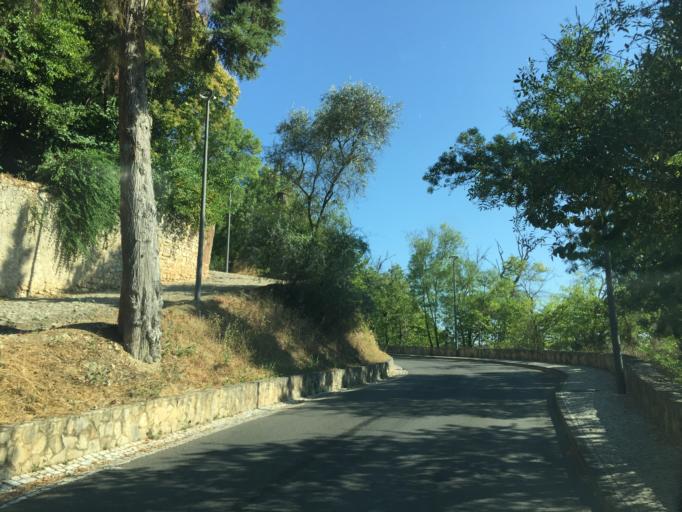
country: PT
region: Santarem
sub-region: Tomar
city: Tomar
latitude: 39.6030
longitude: -8.4160
